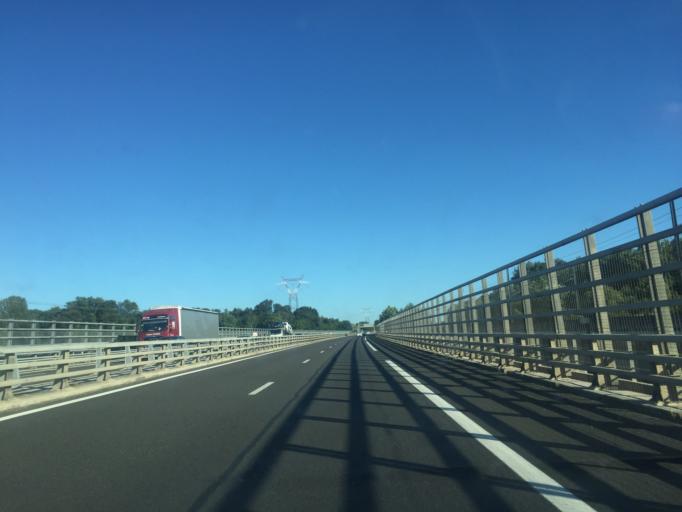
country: FR
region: Rhone-Alpes
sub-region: Departement du Rhone
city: Jons
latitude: 45.8103
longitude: 5.0618
